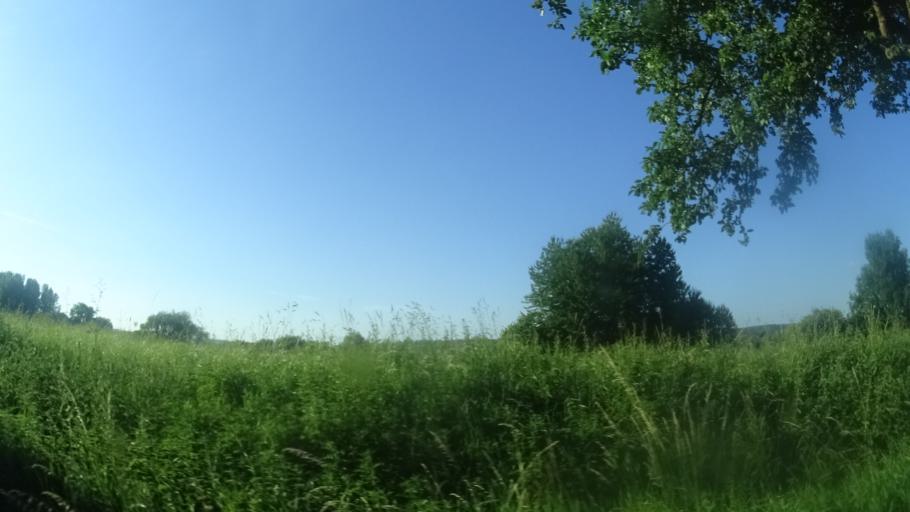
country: DE
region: Lower Saxony
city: Baddeckenstedt
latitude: 52.0858
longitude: 10.2095
